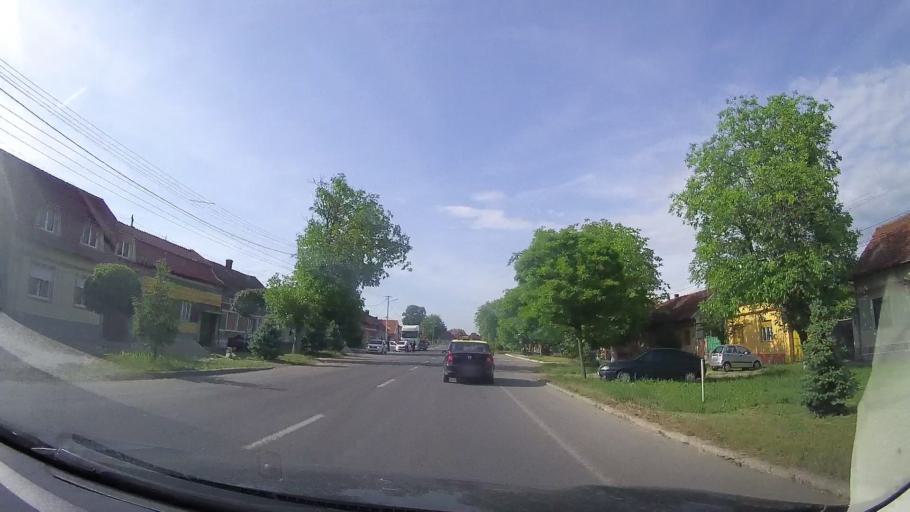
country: RO
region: Caras-Severin
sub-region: Municipiul Caransebes
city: Caransebes
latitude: 45.4005
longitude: 22.2246
